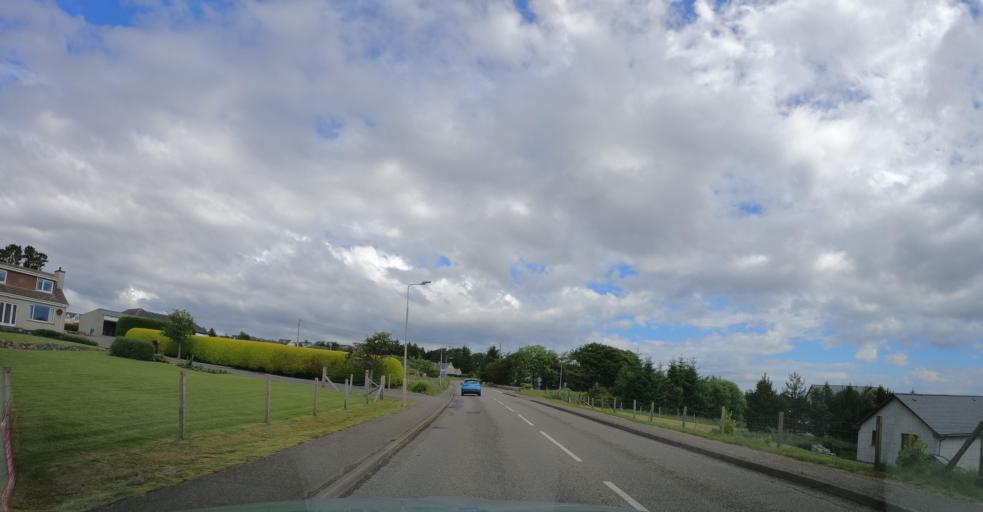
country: GB
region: Scotland
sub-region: Eilean Siar
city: Isle of Lewis
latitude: 58.2330
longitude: -6.3902
